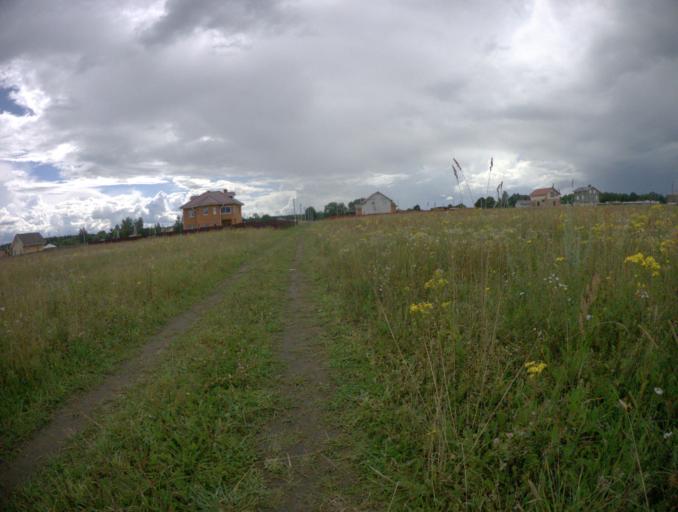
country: RU
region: Vladimir
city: Bogolyubovo
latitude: 56.1153
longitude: 40.5351
